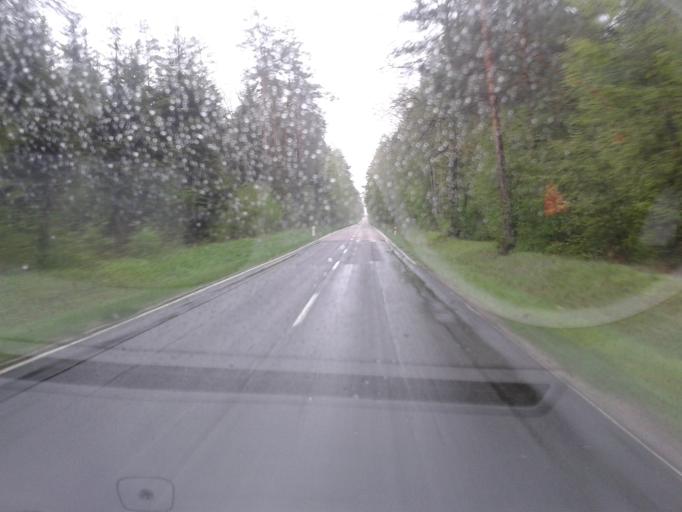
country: PL
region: Subcarpathian Voivodeship
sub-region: Powiat lubaczowski
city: Nowe Siolo
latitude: 50.2979
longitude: 23.2110
